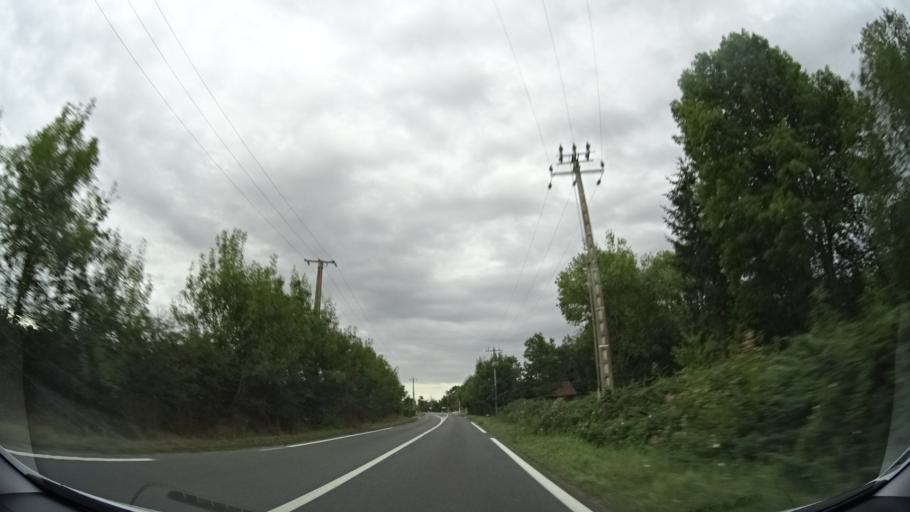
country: FR
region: Centre
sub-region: Departement du Loiret
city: Amilly
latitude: 47.9605
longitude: 2.7957
